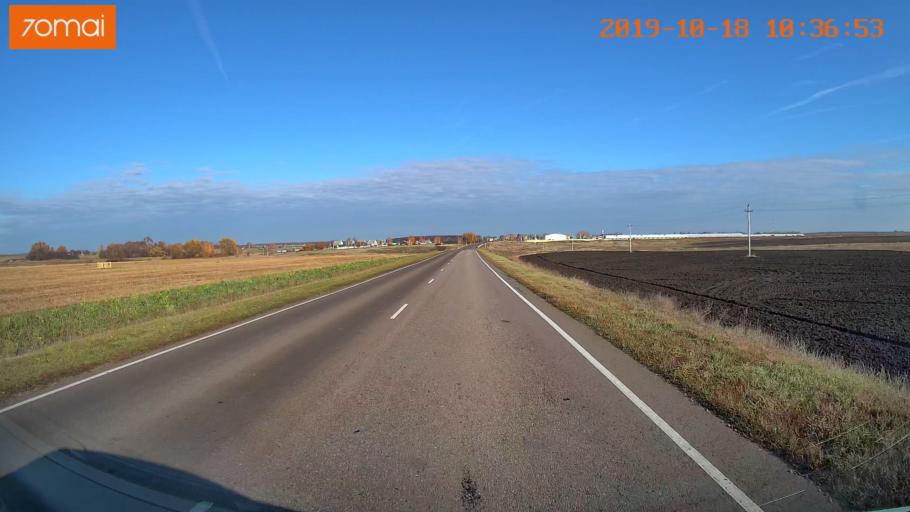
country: RU
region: Tula
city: Kurkino
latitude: 53.5553
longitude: 38.6283
